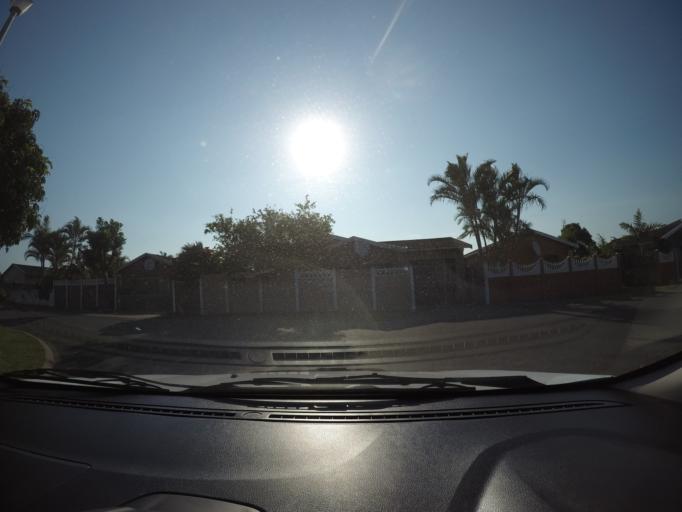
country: ZA
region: KwaZulu-Natal
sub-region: uThungulu District Municipality
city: Richards Bay
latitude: -28.7132
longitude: 32.0381
